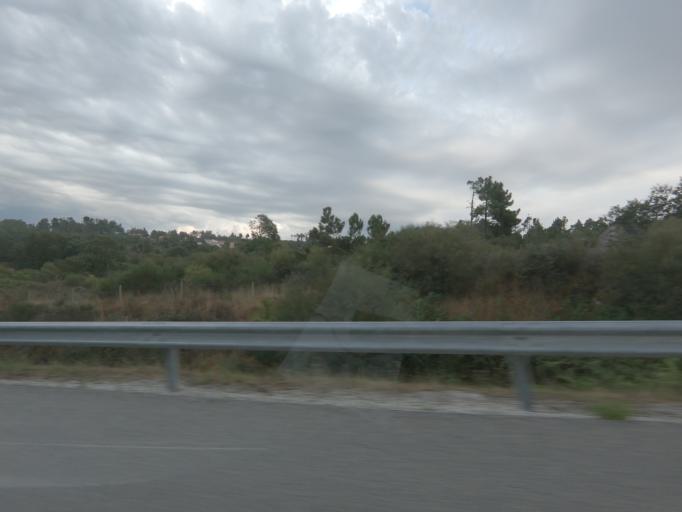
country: PT
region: Viseu
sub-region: Lamego
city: Lamego
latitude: 41.0598
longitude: -7.8333
